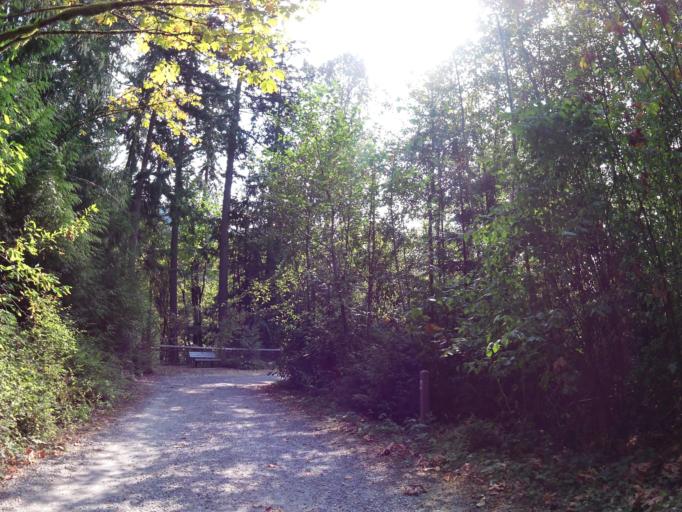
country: US
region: Washington
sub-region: Whatcom County
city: Bellingham
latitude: 48.7028
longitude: -122.4863
